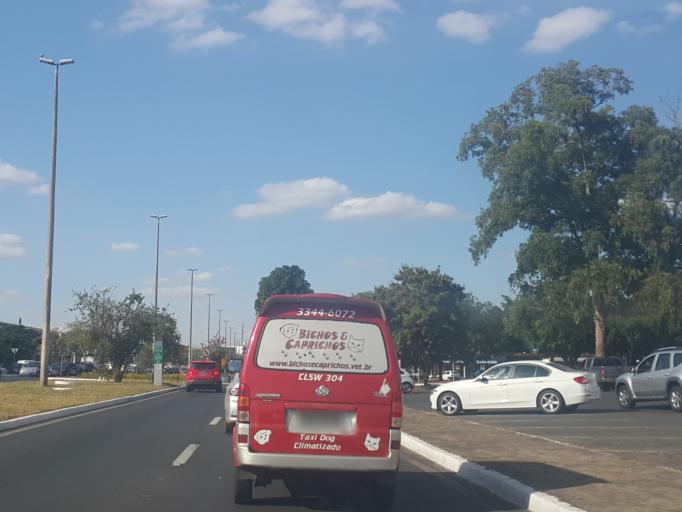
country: BR
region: Federal District
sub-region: Brasilia
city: Brasilia
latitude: -15.7992
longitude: -47.9223
